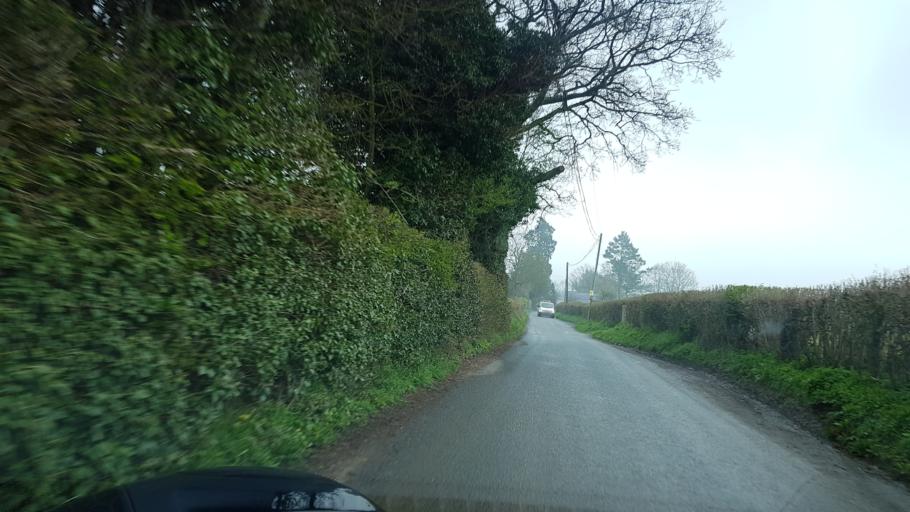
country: GB
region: England
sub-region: Herefordshire
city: Brockhampton
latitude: 52.0125
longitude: -2.5822
